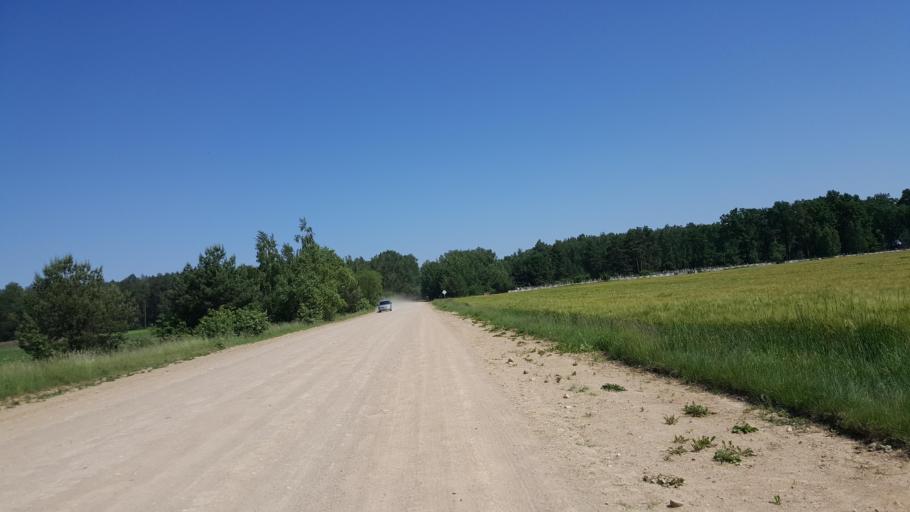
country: BY
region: Brest
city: Zhabinka
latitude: 52.2419
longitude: 24.0080
